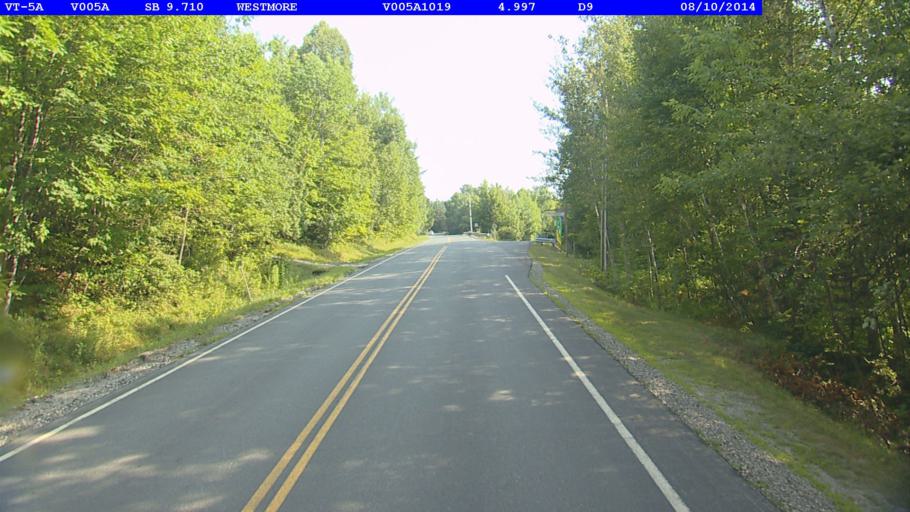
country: US
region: Vermont
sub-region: Orleans County
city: Newport
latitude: 44.7624
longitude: -72.0527
